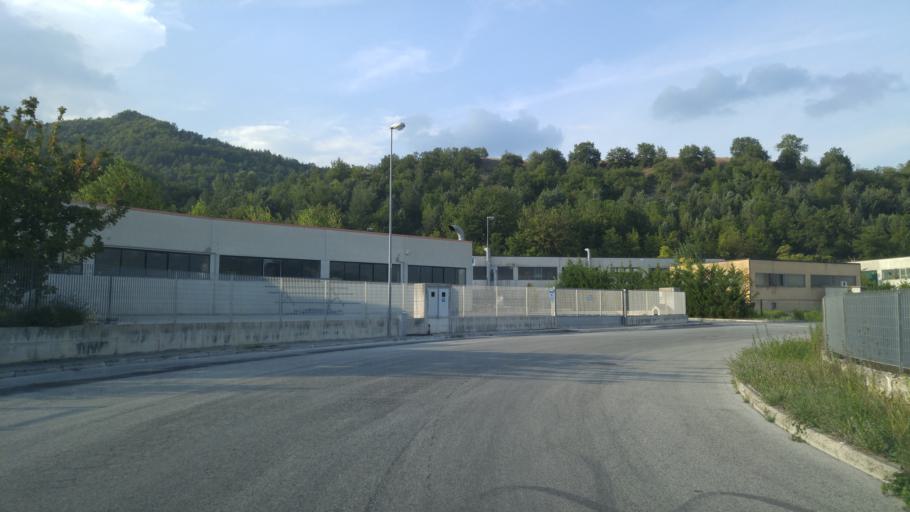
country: IT
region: The Marches
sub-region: Provincia di Pesaro e Urbino
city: Acqualagna
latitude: 43.6291
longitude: 12.6793
